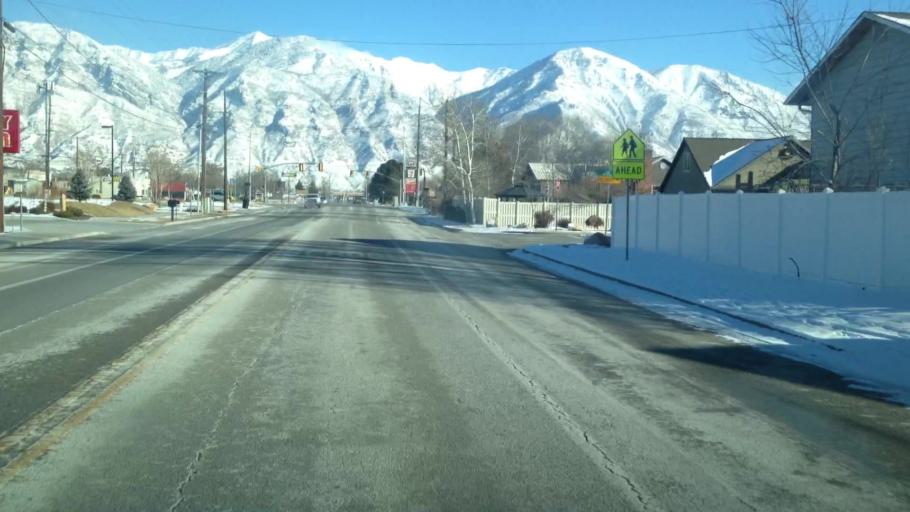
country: US
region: Utah
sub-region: Utah County
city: Provo
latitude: 40.2338
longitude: -111.6967
